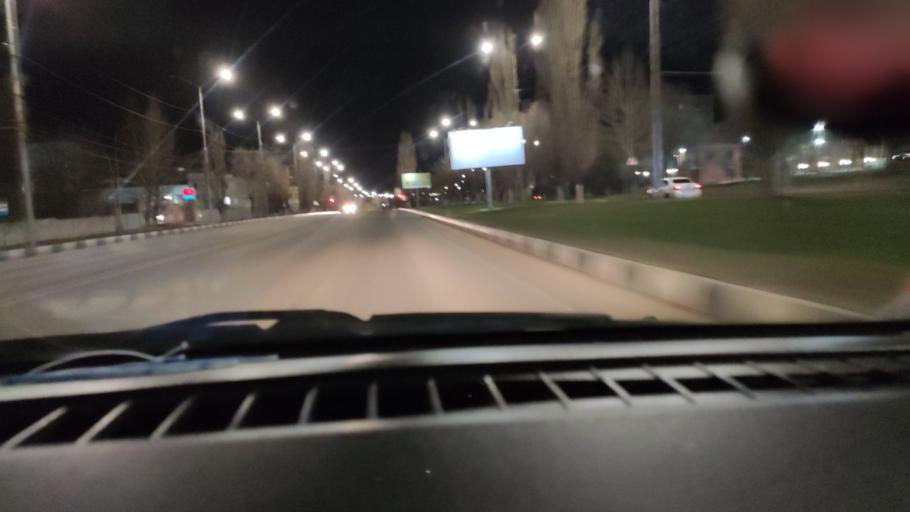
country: RU
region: Saratov
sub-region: Saratovskiy Rayon
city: Saratov
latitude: 51.6076
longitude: 45.9693
